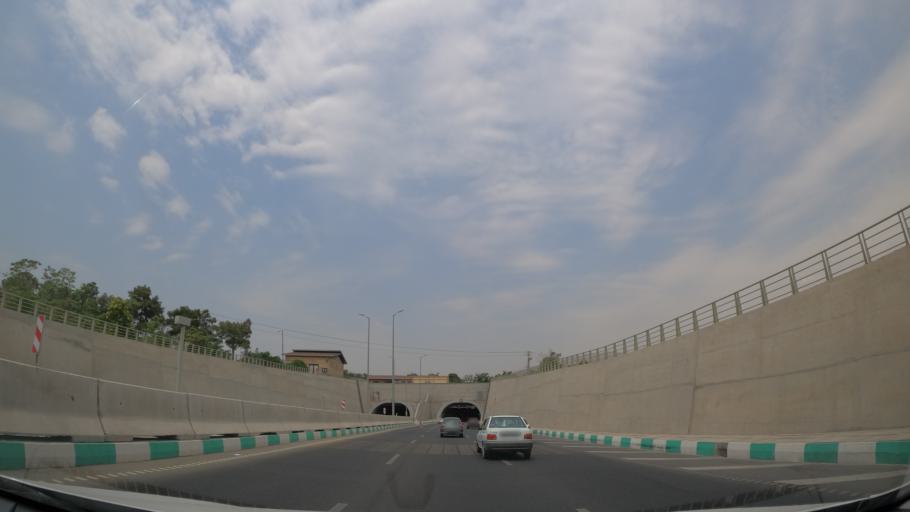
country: IR
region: Tehran
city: Shahr-e Qods
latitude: 35.7403
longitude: 51.2105
